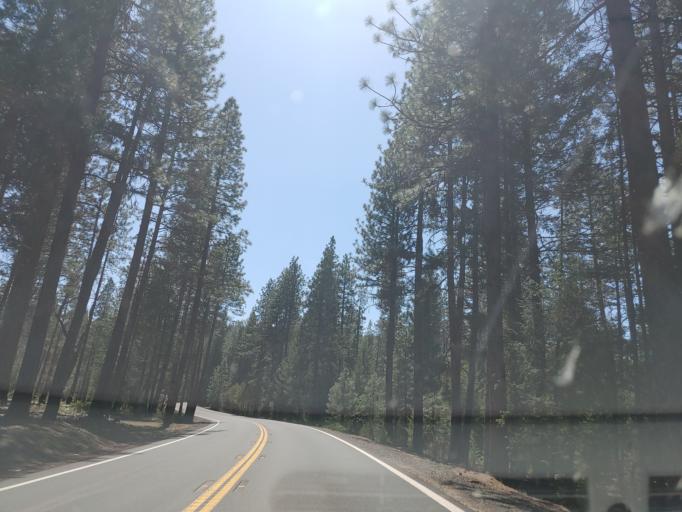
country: US
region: California
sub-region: Shasta County
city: Burney
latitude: 41.0138
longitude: -121.6487
